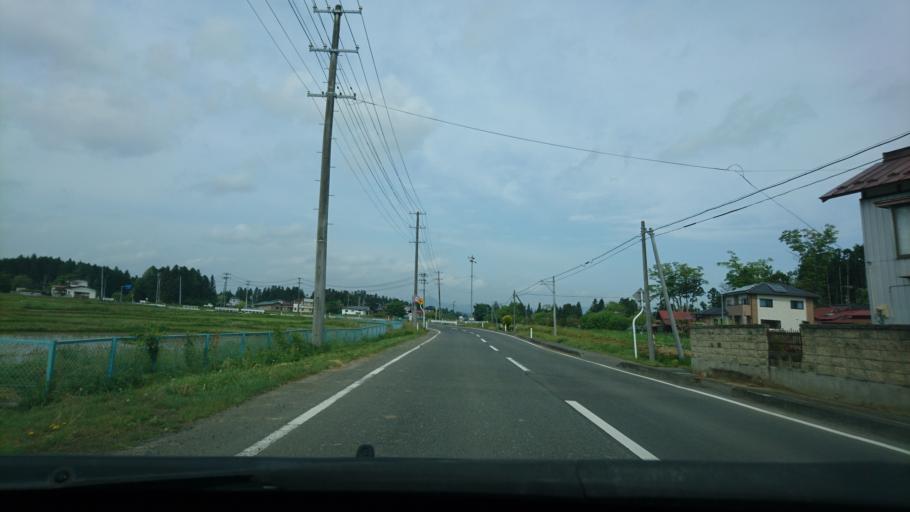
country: JP
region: Iwate
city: Ichinoseki
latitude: 38.8274
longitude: 141.0267
